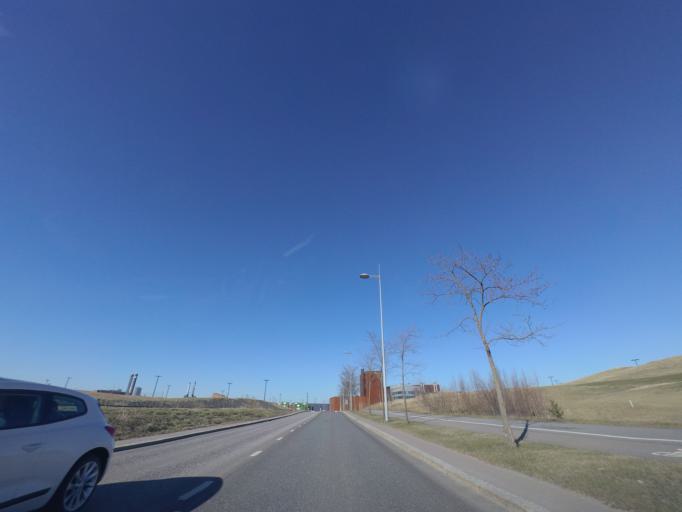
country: FI
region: Uusimaa
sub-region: Helsinki
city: Vantaa
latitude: 60.2116
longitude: 25.1653
